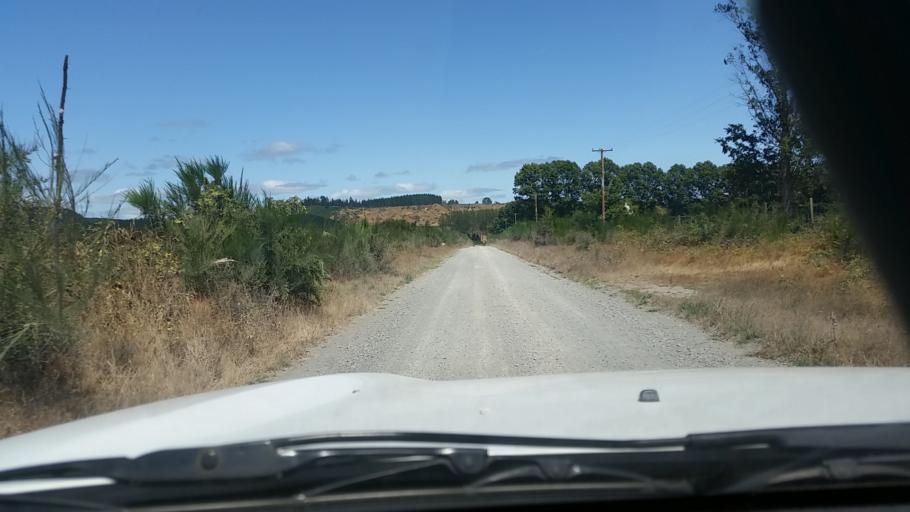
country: NZ
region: Bay of Plenty
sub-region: Whakatane District
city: Murupara
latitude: -38.3358
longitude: 176.5606
